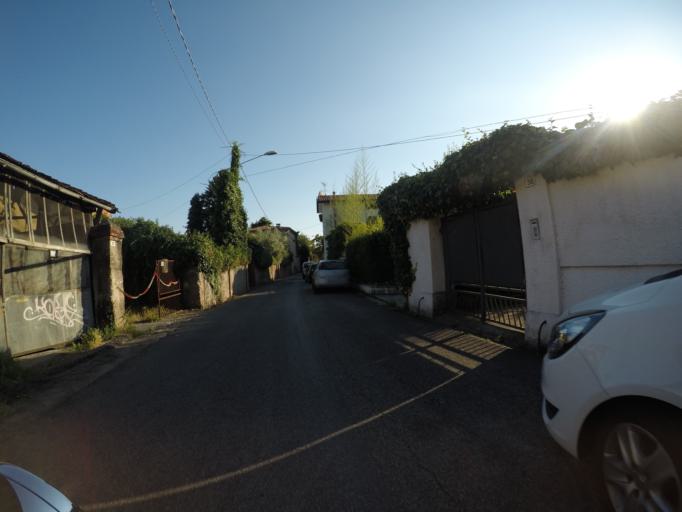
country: IT
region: Tuscany
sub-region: Provincia di Massa-Carrara
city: Massa
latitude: 44.0301
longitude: 10.1357
